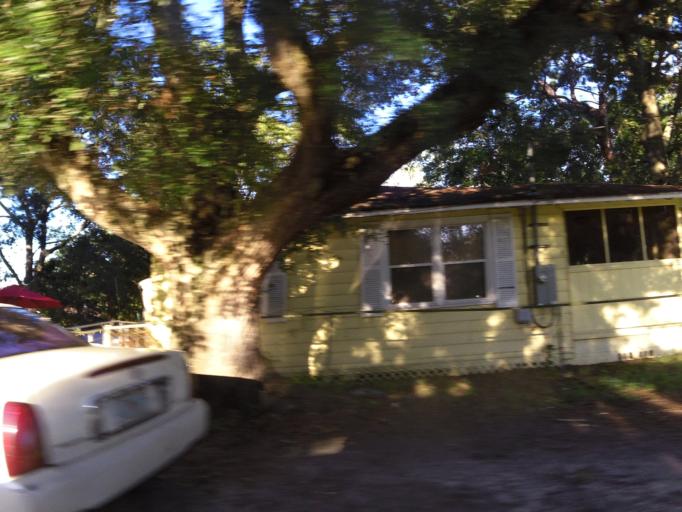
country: US
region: Florida
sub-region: Duval County
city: Jacksonville
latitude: 30.3521
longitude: -81.6999
